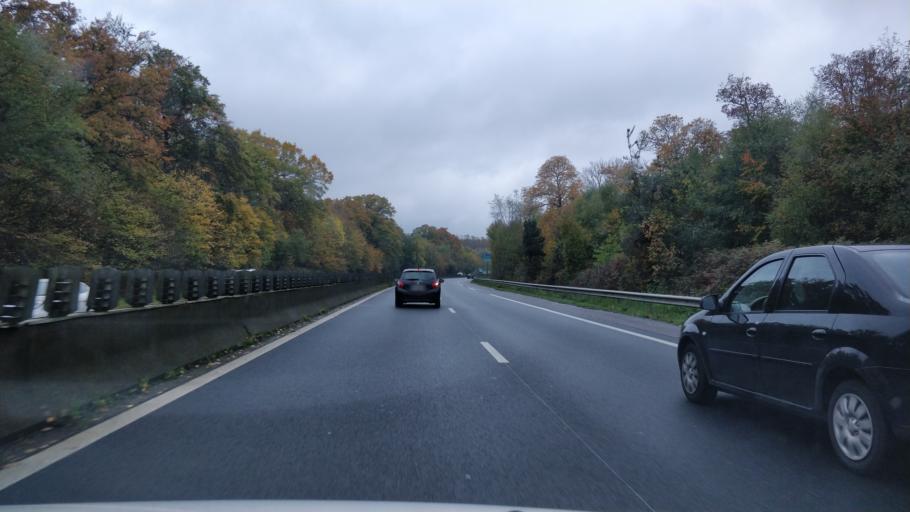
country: FR
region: Haute-Normandie
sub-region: Departement de la Seine-Maritime
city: Grand-Couronne
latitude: 49.3469
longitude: 1.0179
